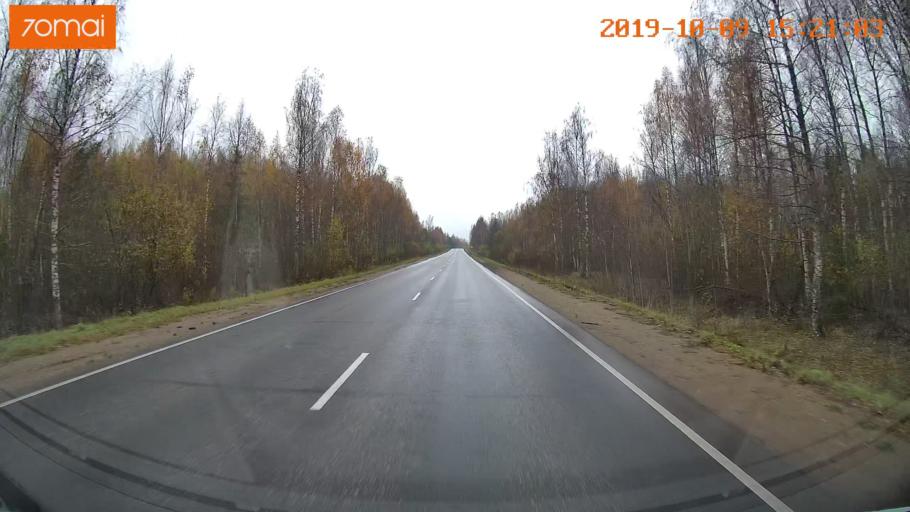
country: RU
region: Kostroma
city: Susanino
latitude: 58.0577
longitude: 41.5269
